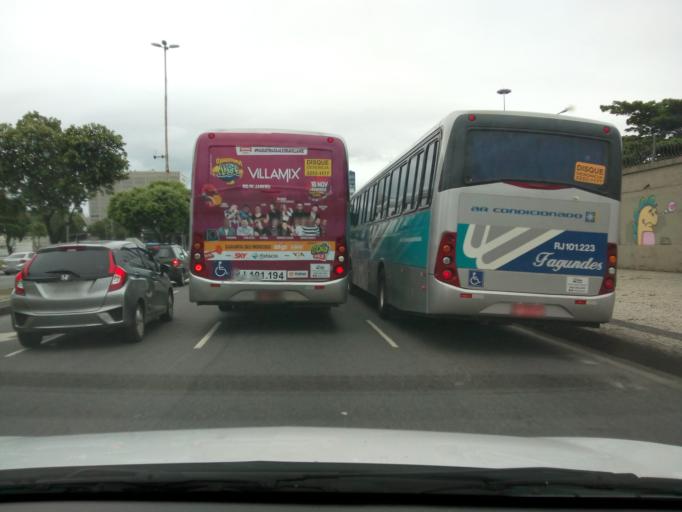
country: BR
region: Rio de Janeiro
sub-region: Rio De Janeiro
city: Rio de Janeiro
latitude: -22.9063
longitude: -43.1952
